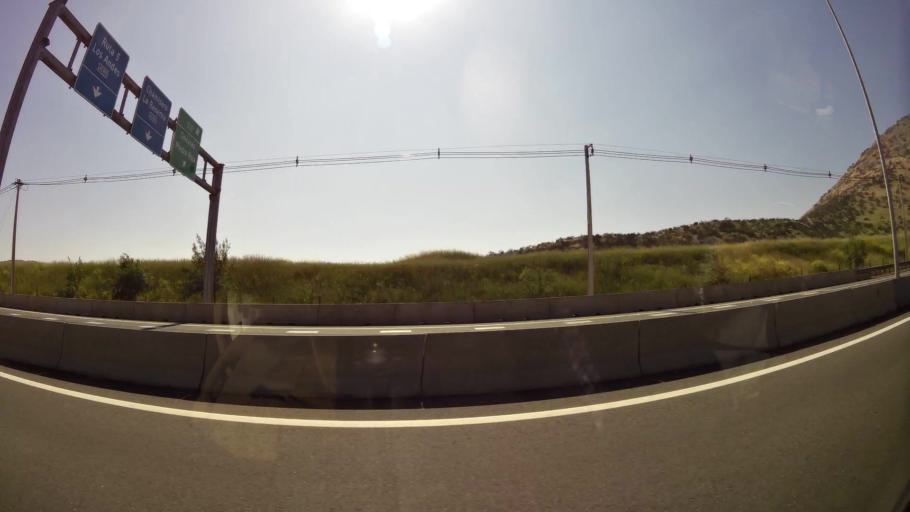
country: CL
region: Santiago Metropolitan
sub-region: Provincia de Chacabuco
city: Chicureo Abajo
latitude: -33.3033
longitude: -70.6564
